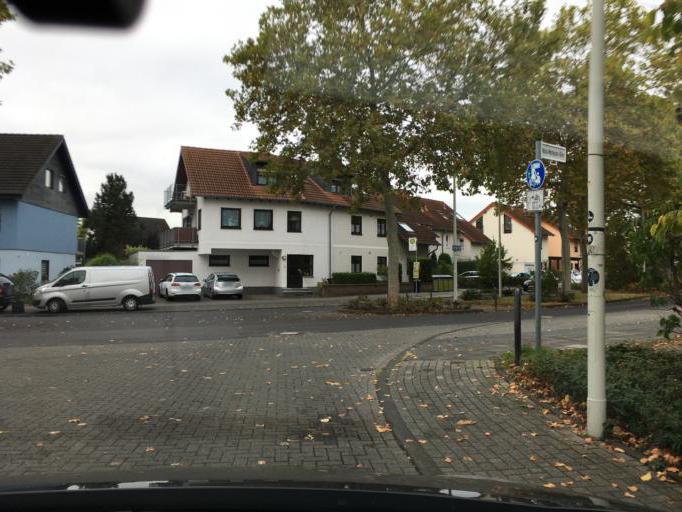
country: DE
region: North Rhine-Westphalia
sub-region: Regierungsbezirk Koln
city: Bonn
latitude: 50.7473
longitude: 7.1389
